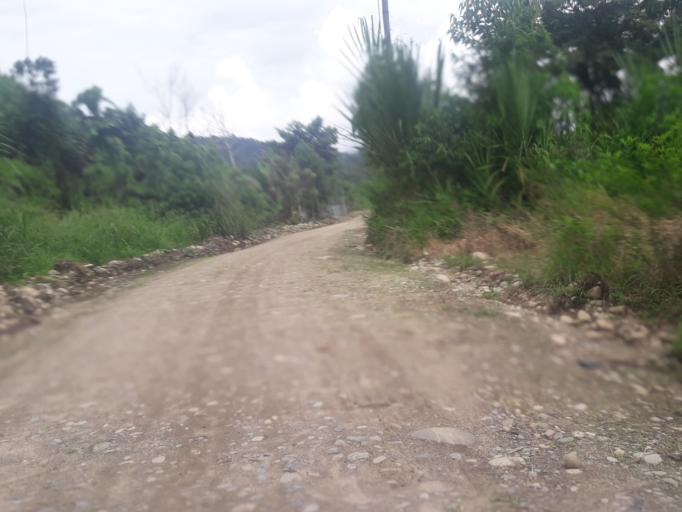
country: EC
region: Napo
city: Tena
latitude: -0.9750
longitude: -77.8454
